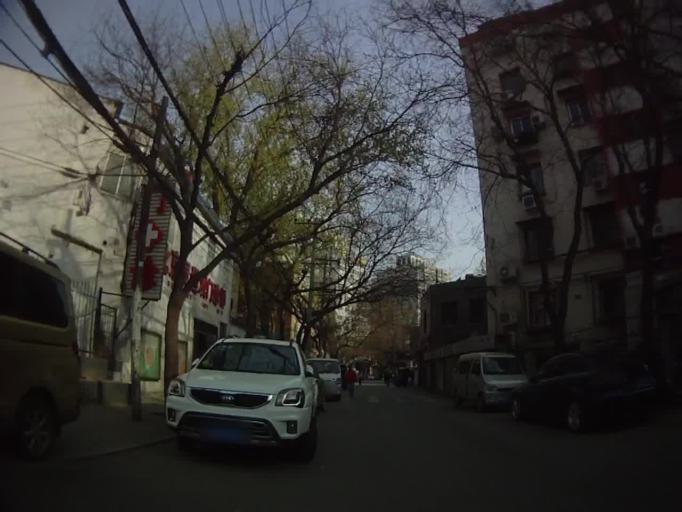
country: CN
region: Beijing
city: Chaowai
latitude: 39.9049
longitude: 116.4407
